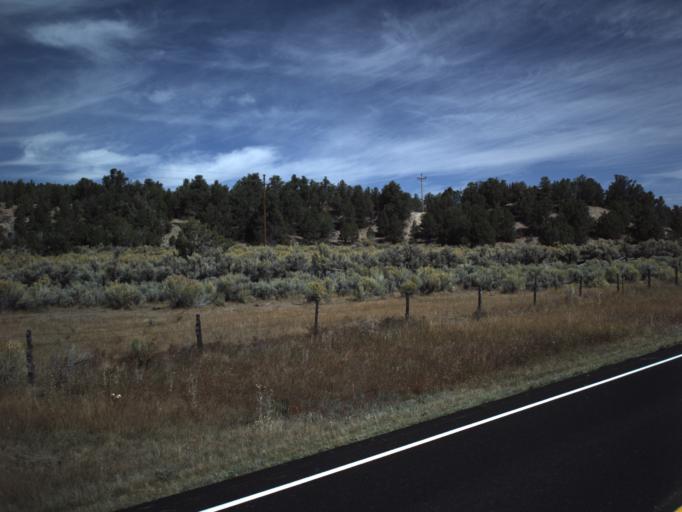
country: US
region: Utah
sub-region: Garfield County
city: Panguitch
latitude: 37.6942
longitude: -111.7964
